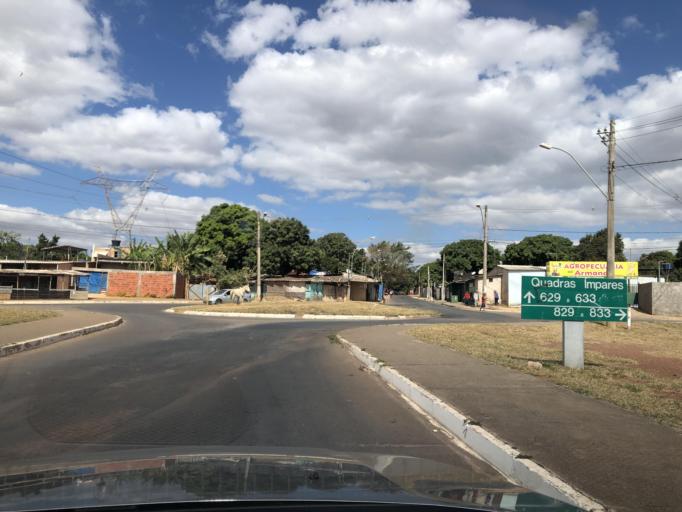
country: BR
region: Federal District
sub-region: Brasilia
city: Brasilia
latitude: -15.8868
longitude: -48.1437
